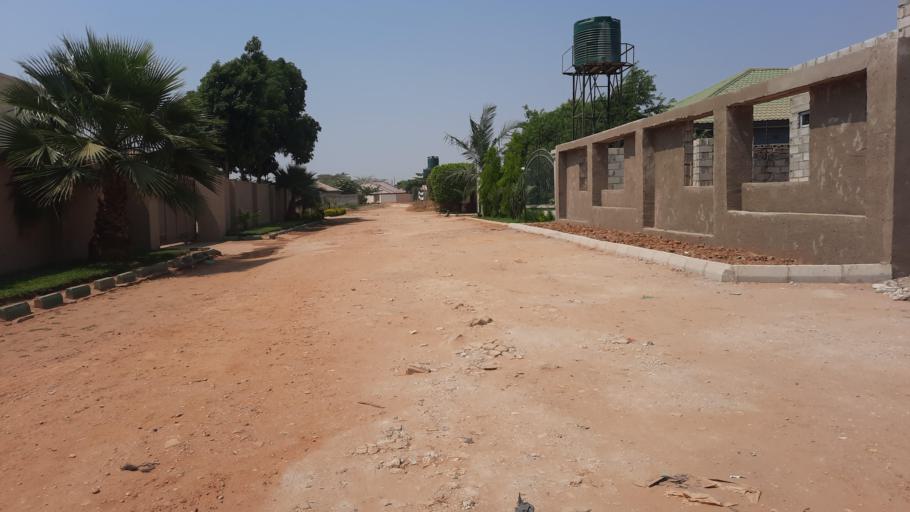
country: ZM
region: Lusaka
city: Lusaka
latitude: -15.3924
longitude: 28.3912
